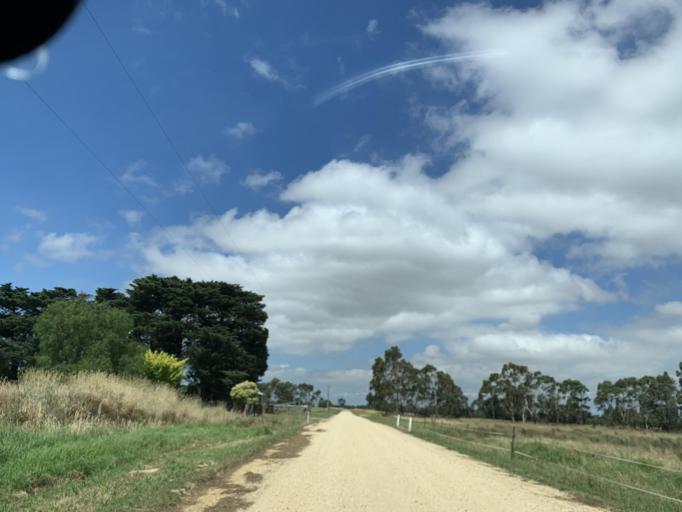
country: AU
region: Victoria
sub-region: Latrobe
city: Traralgon
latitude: -38.0924
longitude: 146.5914
